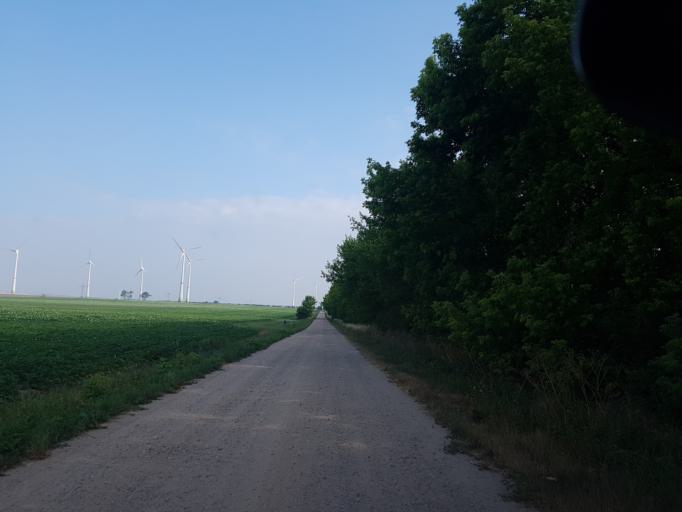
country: DE
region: Saxony-Anhalt
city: Zahna
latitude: 51.9821
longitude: 12.8231
